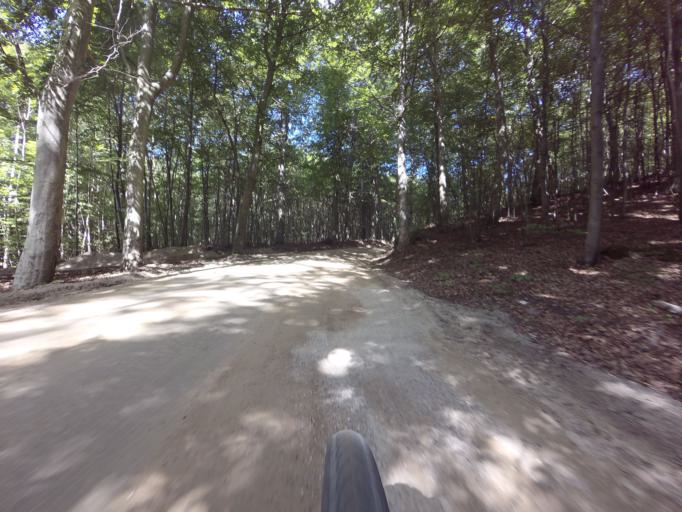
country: DK
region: Zealand
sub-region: Vordingborg Kommune
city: Stege
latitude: 54.9683
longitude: 12.5398
